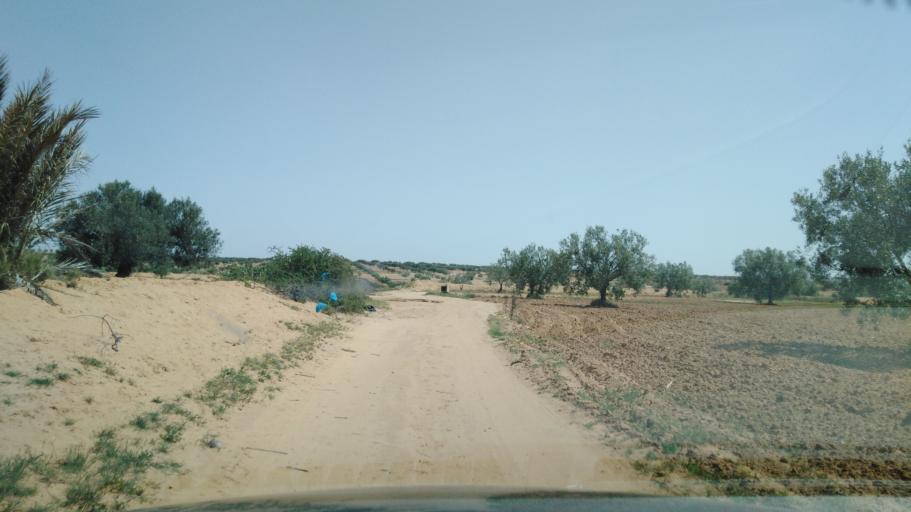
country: TN
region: Safaqis
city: Sfax
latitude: 34.6924
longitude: 10.4525
